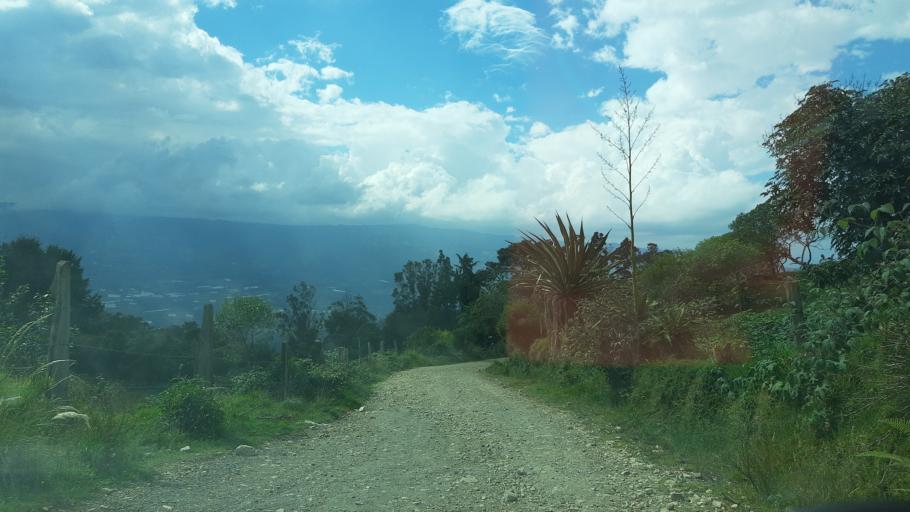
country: CO
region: Boyaca
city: Santa Sofia
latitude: 5.7278
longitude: -73.5534
